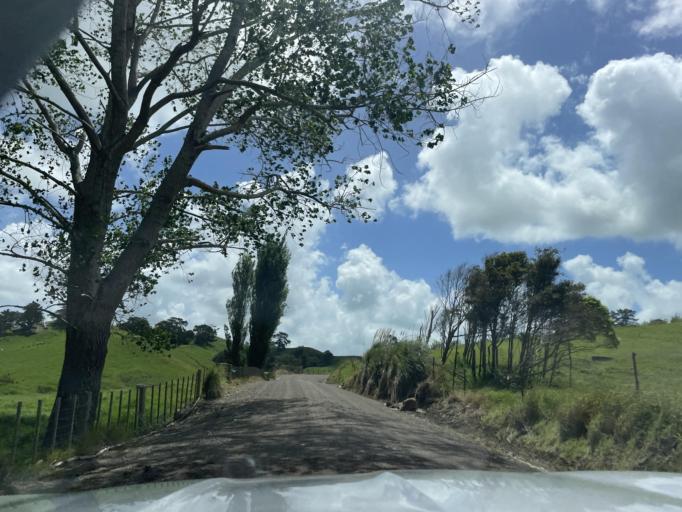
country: NZ
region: Auckland
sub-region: Auckland
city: Wellsford
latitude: -36.1877
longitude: 174.3232
